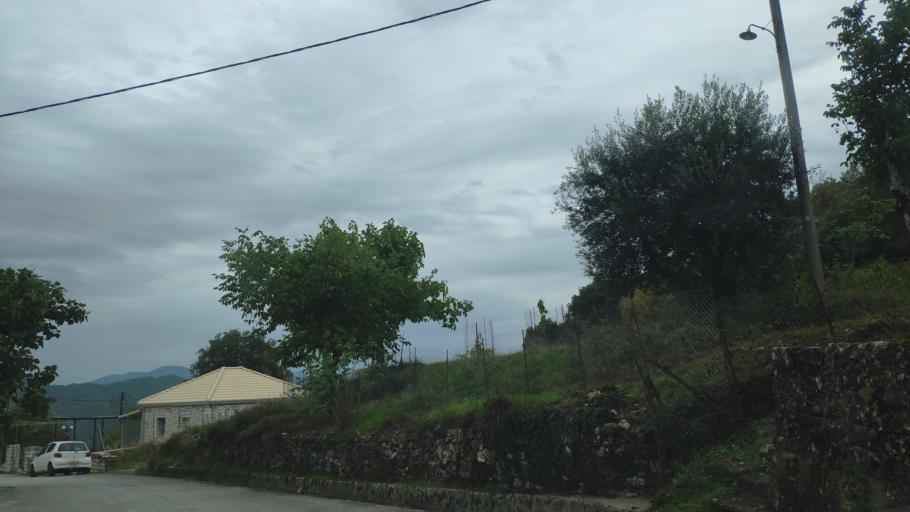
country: GR
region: Epirus
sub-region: Nomos Thesprotias
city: Paramythia
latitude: 39.4579
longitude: 20.6722
